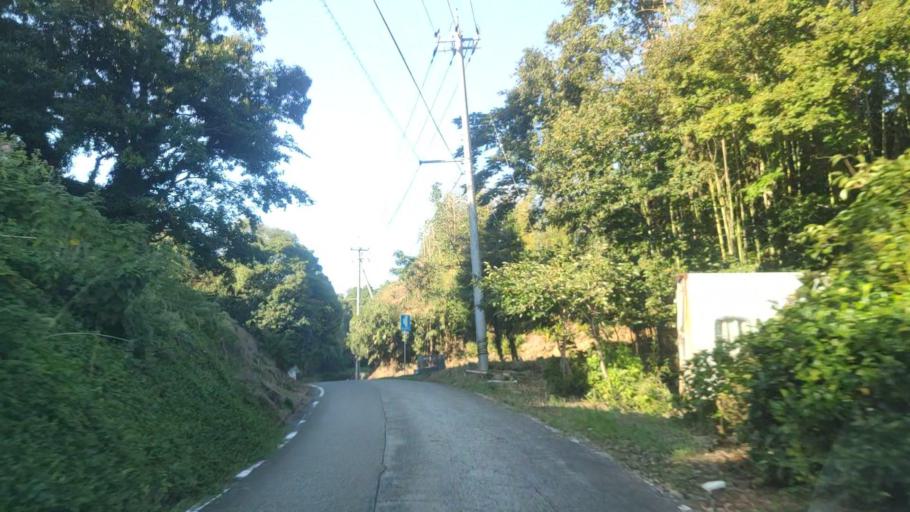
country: JP
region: Ishikawa
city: Nanao
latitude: 37.1197
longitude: 136.8940
